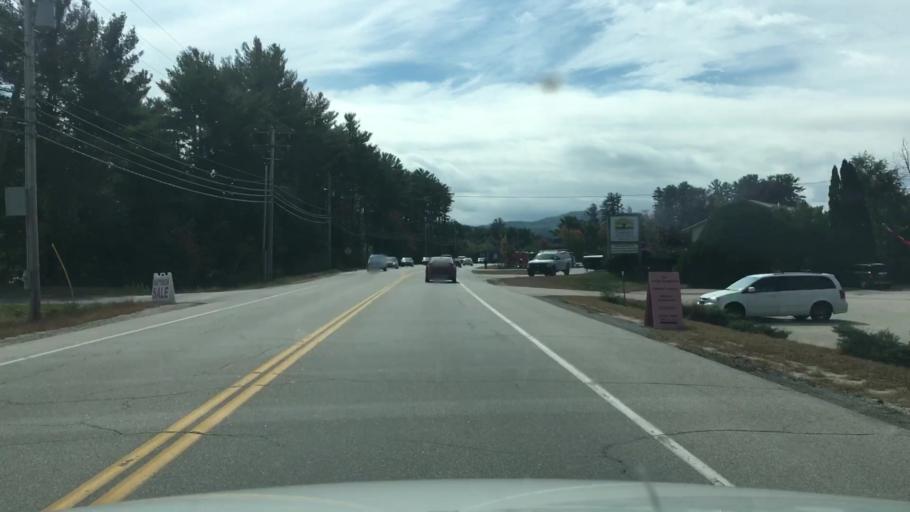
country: US
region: New Hampshire
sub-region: Carroll County
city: Conway
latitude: 43.9875
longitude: -71.1109
